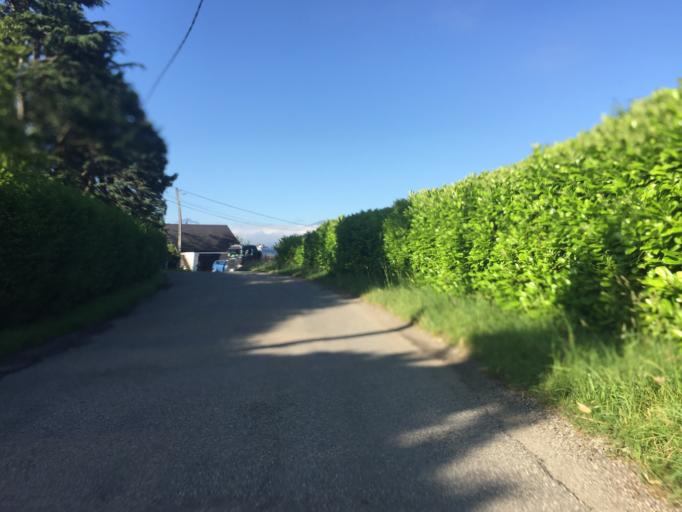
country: FR
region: Rhone-Alpes
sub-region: Departement de la Savoie
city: Drumettaz-Clarafond
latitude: 45.6655
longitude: 5.9323
